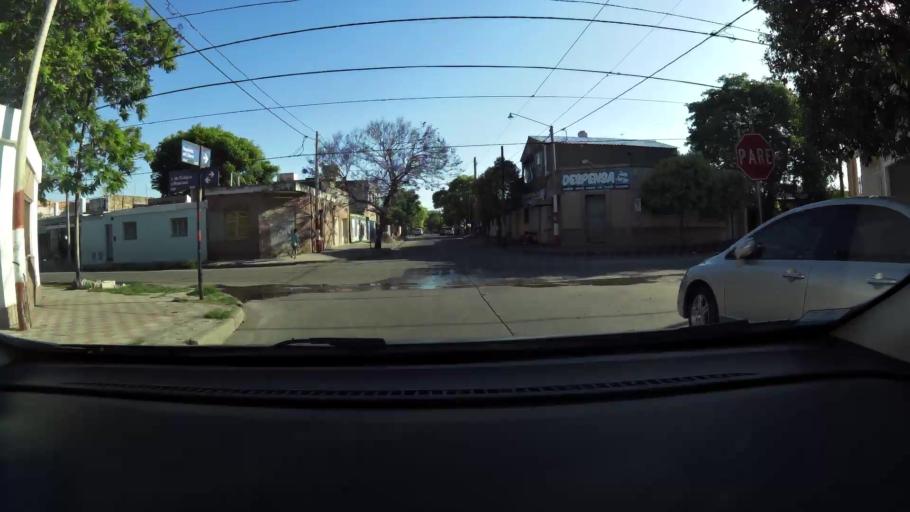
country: AR
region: Cordoba
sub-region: Departamento de Capital
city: Cordoba
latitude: -31.3842
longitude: -64.1696
